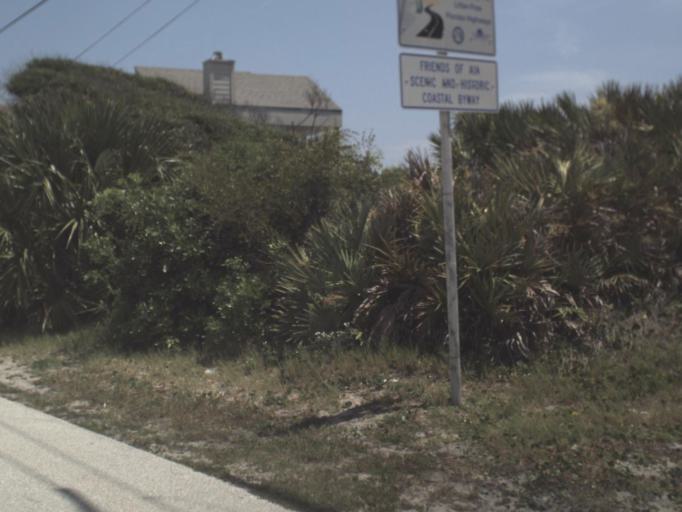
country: US
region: Florida
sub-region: Saint Johns County
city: Villano Beach
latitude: 29.9744
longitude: -81.3111
